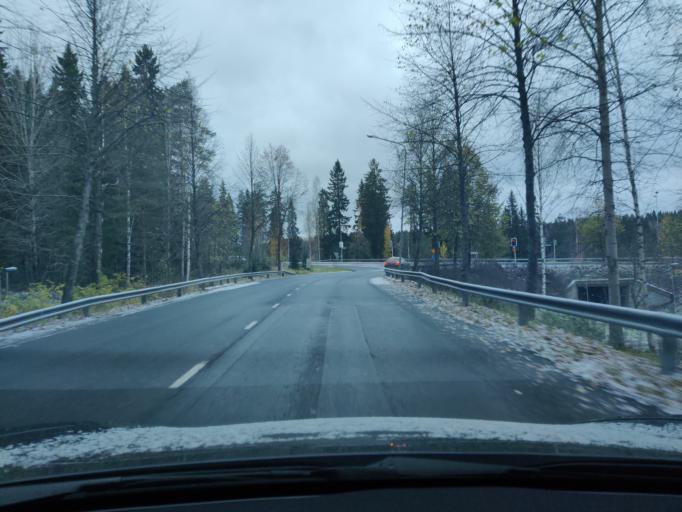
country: FI
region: Northern Savo
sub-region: Kuopio
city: Kuopio
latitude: 62.8415
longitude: 27.6341
